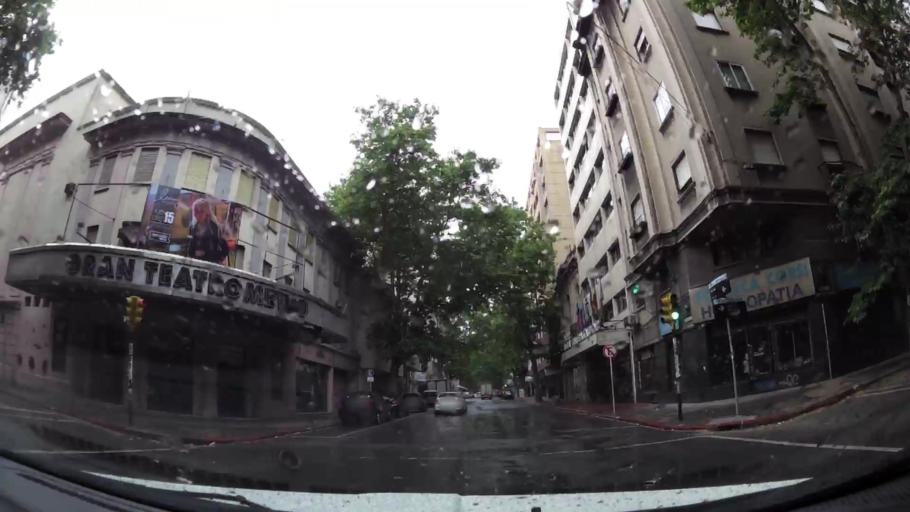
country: UY
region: Montevideo
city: Montevideo
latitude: -34.9066
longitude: -56.1903
